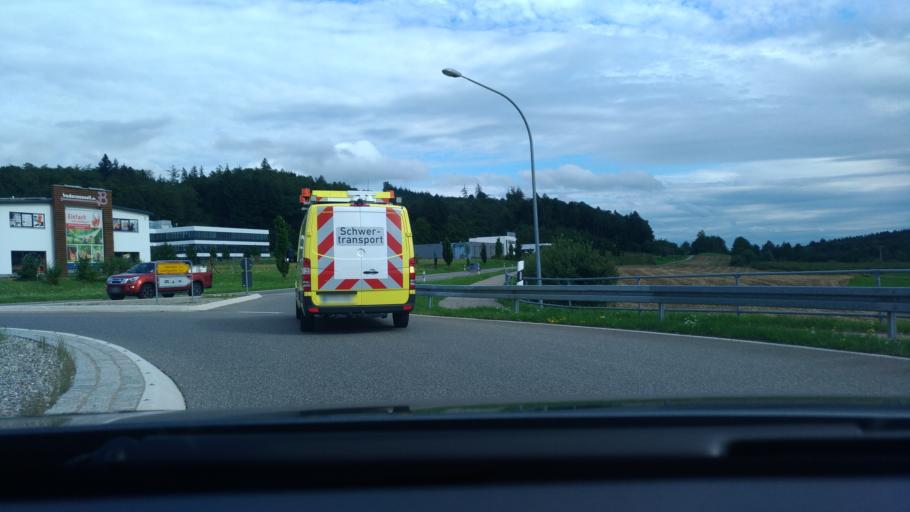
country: DE
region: Baden-Wuerttemberg
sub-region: Freiburg Region
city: Stockach
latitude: 47.8390
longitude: 9.0276
